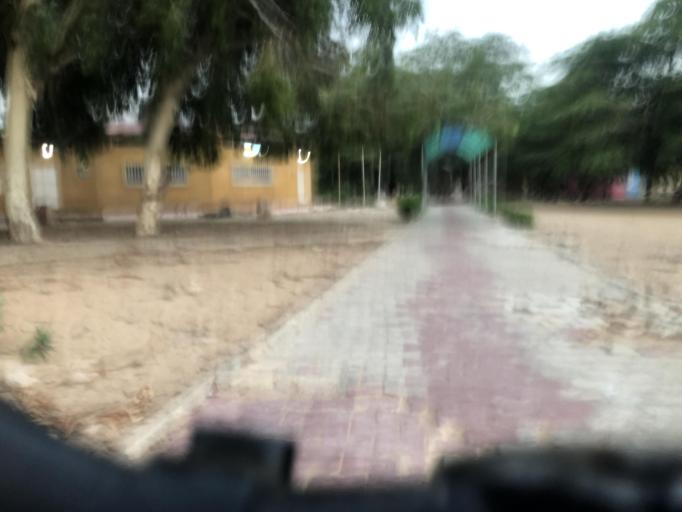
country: SN
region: Saint-Louis
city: Saint-Louis
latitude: 16.0654
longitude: -16.4260
